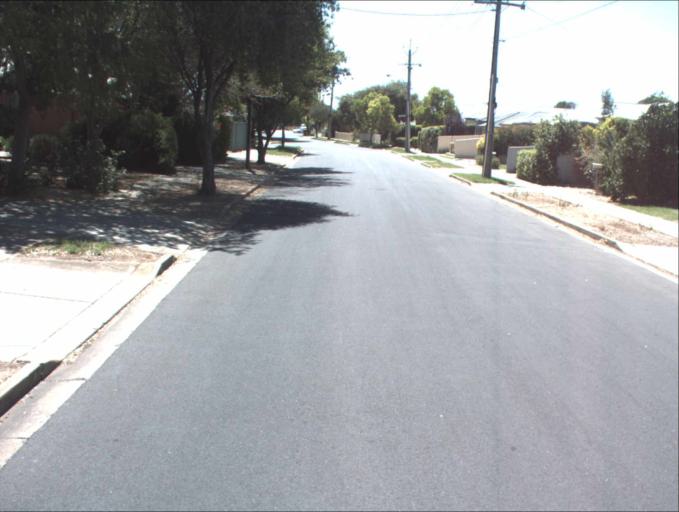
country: AU
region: South Australia
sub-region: Port Adelaide Enfield
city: Blair Athol
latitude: -34.8690
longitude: 138.6124
